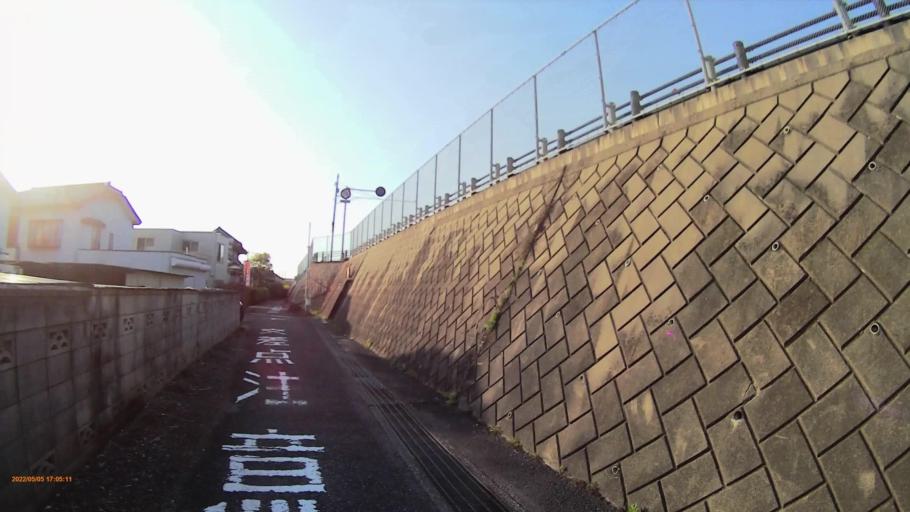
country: JP
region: Saitama
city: Kurihashi
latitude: 36.1198
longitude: 139.7183
